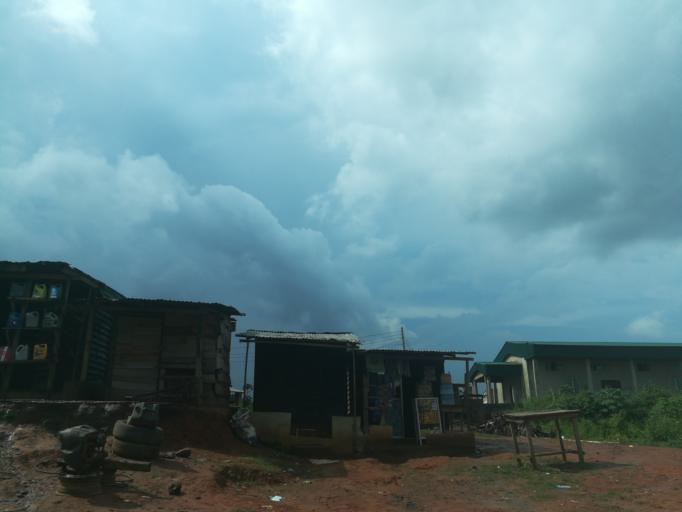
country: NG
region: Lagos
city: Ikorodu
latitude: 6.6462
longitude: 3.5610
